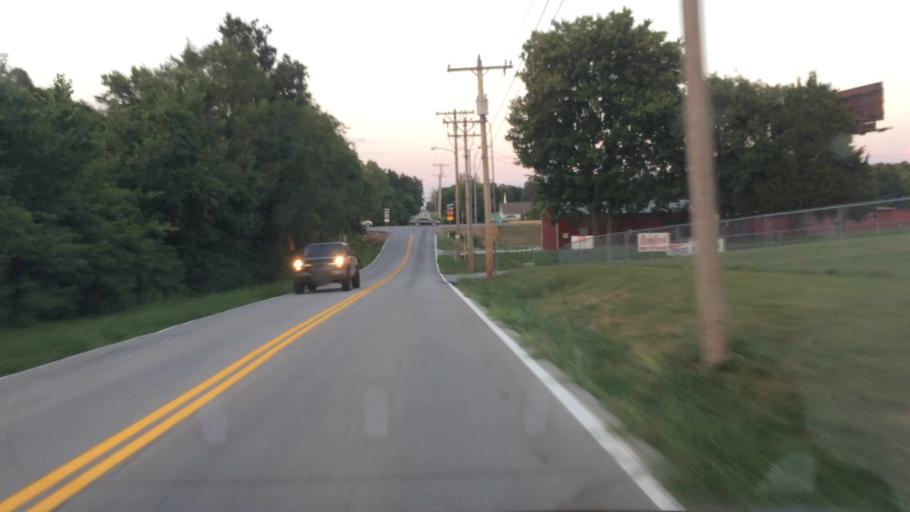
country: US
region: Missouri
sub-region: Greene County
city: Springfield
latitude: 37.1902
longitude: -93.3518
